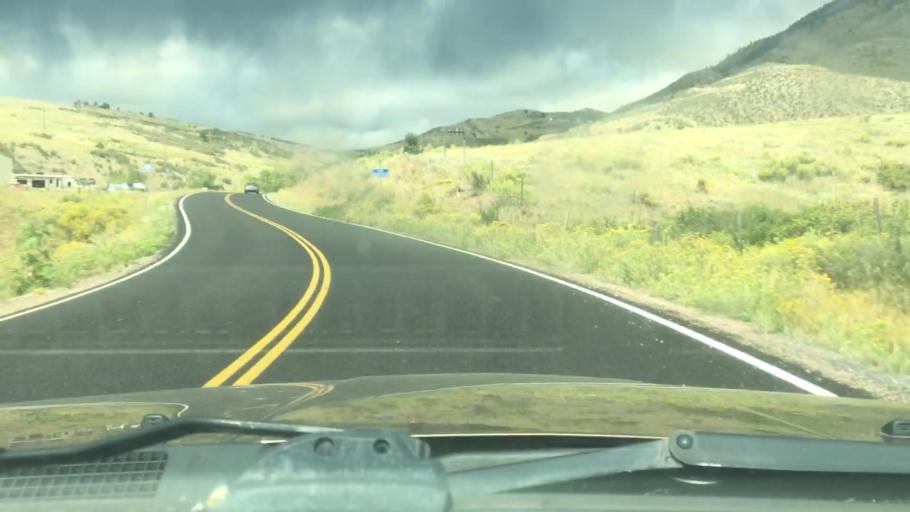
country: US
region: Colorado
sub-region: Larimer County
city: Laporte
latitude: 40.5243
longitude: -105.2594
